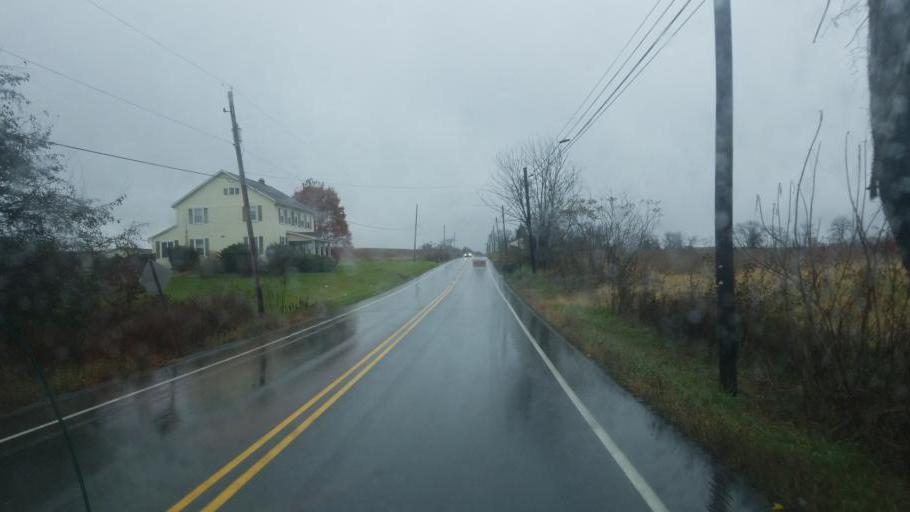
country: US
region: Pennsylvania
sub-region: Clinton County
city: Mill Hall
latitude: 41.0986
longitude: -77.5200
